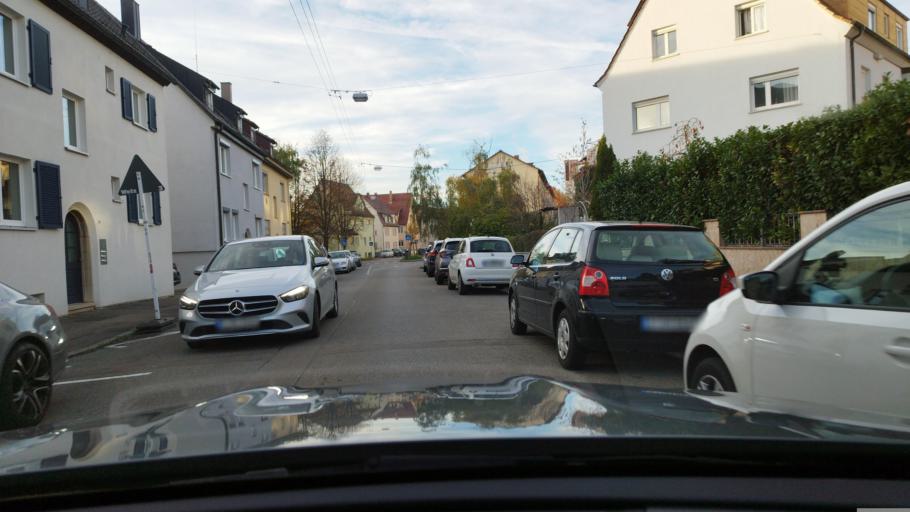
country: DE
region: Baden-Wuerttemberg
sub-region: Regierungsbezirk Stuttgart
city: Stuttgart-Ost
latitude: 48.8034
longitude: 9.2375
